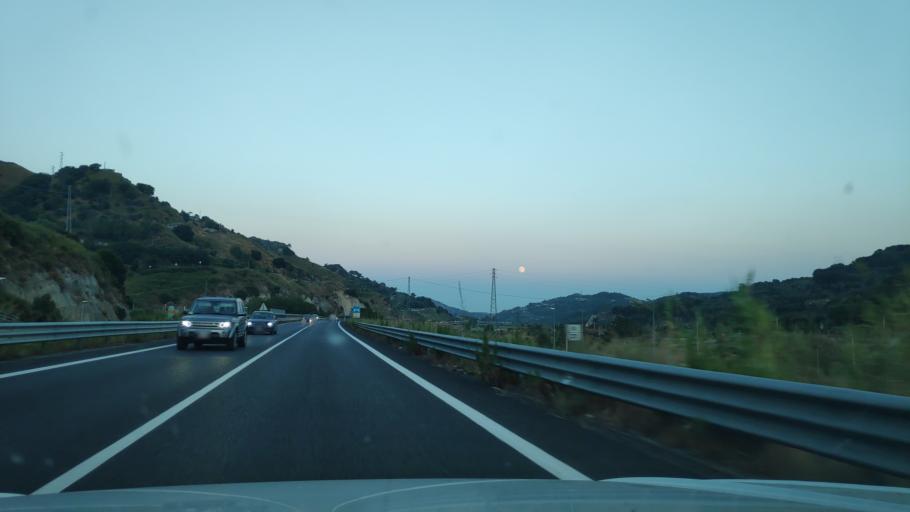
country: IT
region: Calabria
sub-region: Provincia di Reggio Calabria
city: Mammola
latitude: 38.3574
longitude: 16.2348
